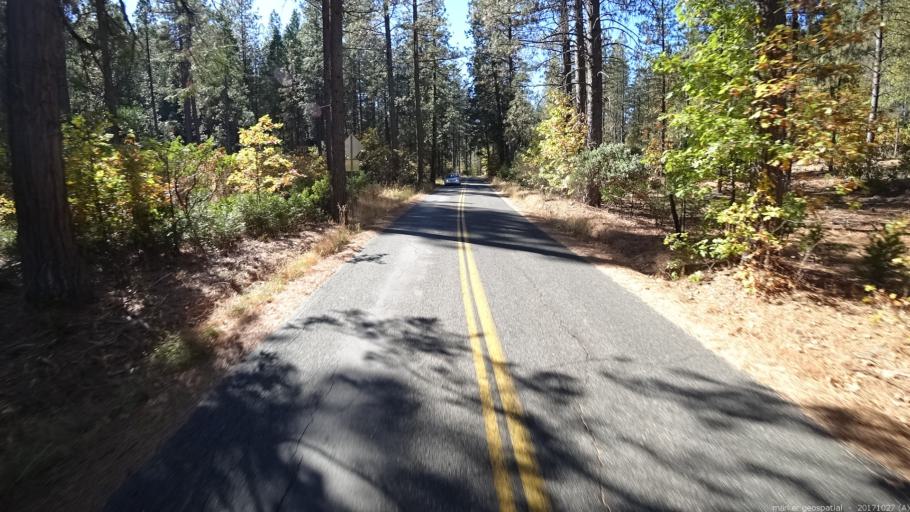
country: US
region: California
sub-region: Shasta County
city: Shingletown
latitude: 40.7218
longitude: -121.9801
